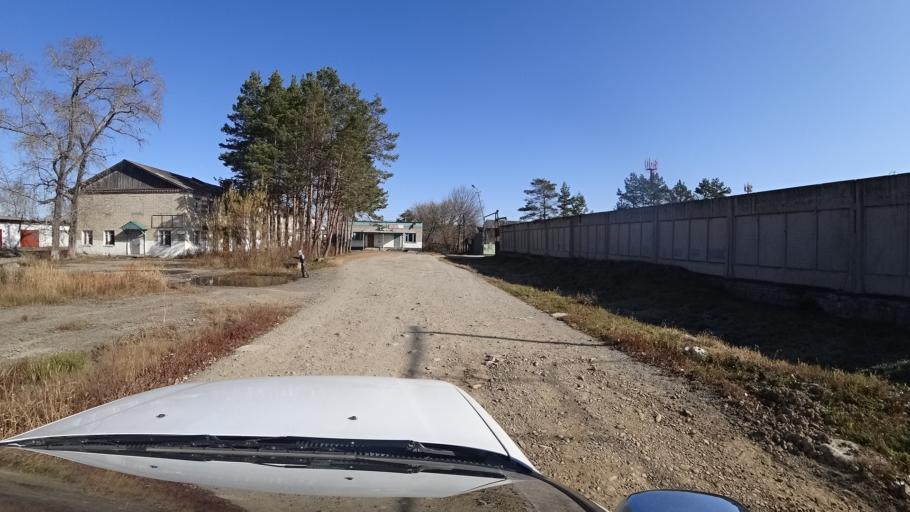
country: RU
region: Primorskiy
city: Dal'nerechensk
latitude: 45.9103
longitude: 133.8043
